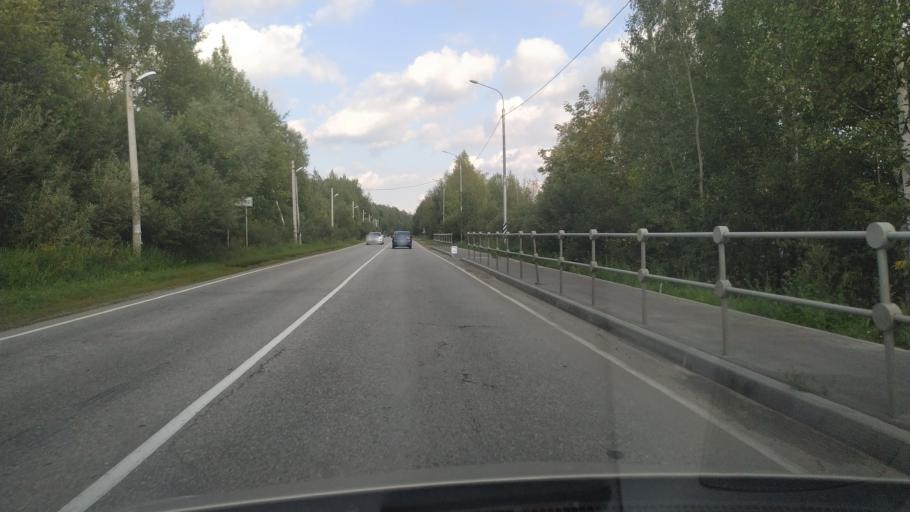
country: RU
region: Moskovskaya
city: Likino-Dulevo
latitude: 55.7295
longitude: 39.0079
